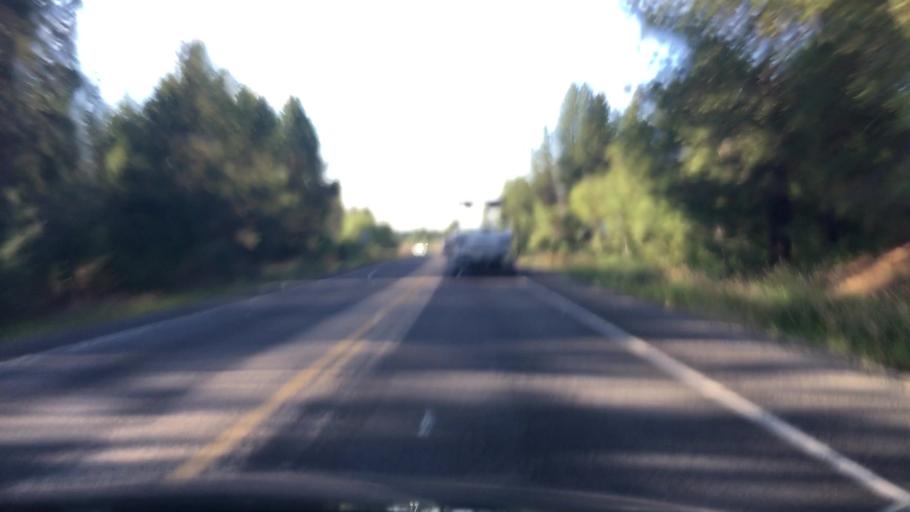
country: US
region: Idaho
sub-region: Valley County
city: Cascade
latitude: 44.6902
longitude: -116.0512
